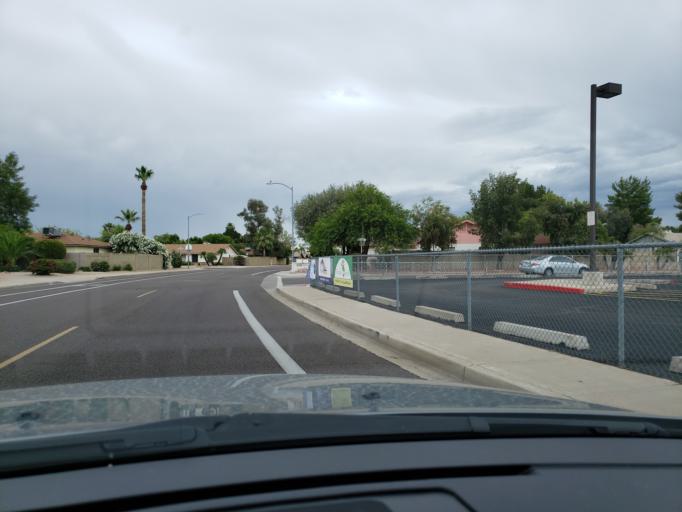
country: US
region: Arizona
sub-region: Maricopa County
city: Paradise Valley
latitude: 33.6213
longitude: -111.9533
